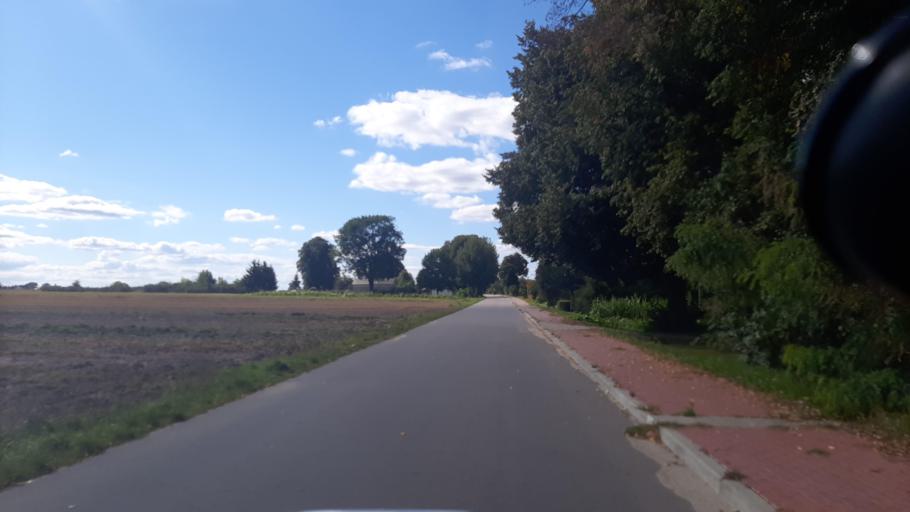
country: PL
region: Lublin Voivodeship
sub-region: Powiat lubelski
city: Garbow
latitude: 51.4029
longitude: 22.3469
